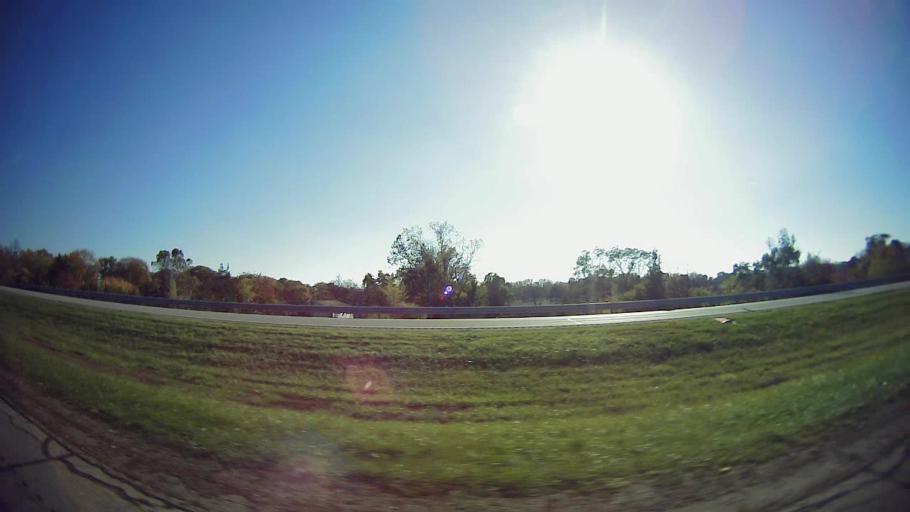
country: US
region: Michigan
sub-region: Oakland County
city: Farmington
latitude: 42.4584
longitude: -83.3893
